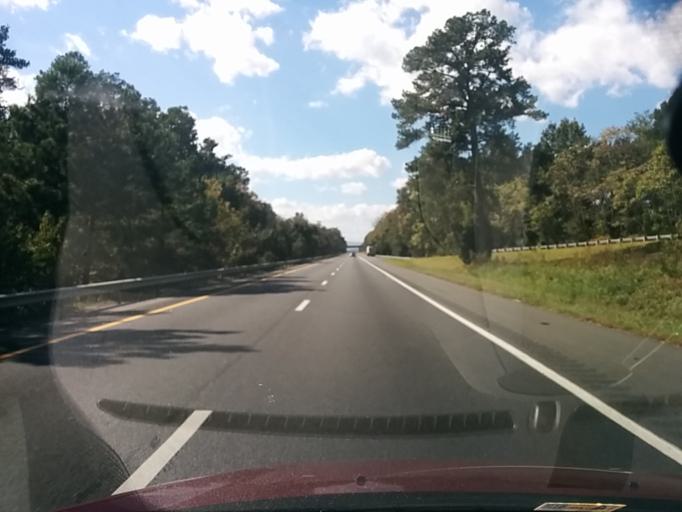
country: US
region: Virginia
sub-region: Albemarle County
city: Crozet
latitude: 38.0341
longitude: -78.6296
